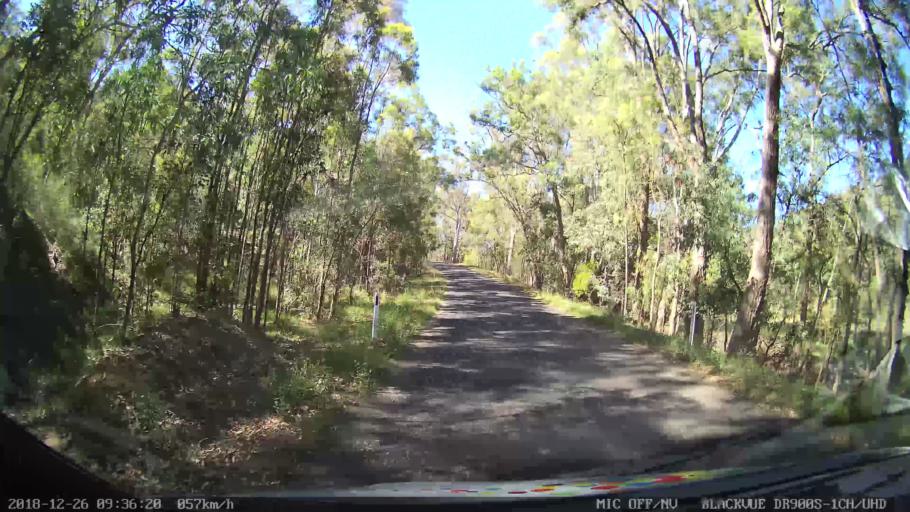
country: AU
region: New South Wales
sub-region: Mid-Western Regional
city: Kandos
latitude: -32.9230
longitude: 150.0401
